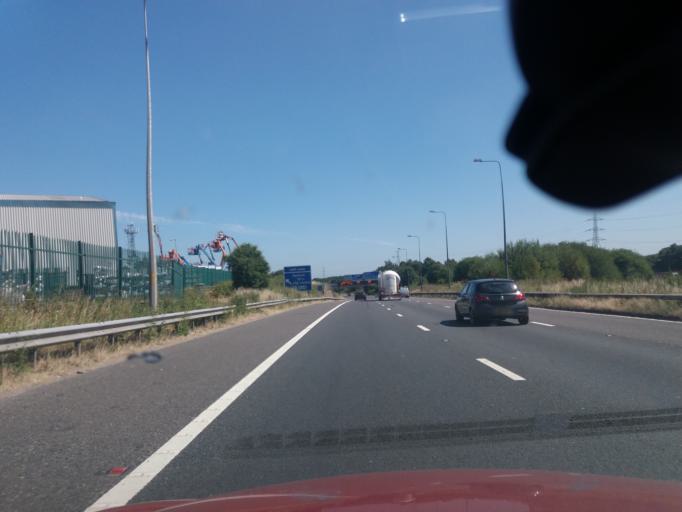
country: GB
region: England
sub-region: Borough of Bolton
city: Kearsley
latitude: 53.5358
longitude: -2.3907
